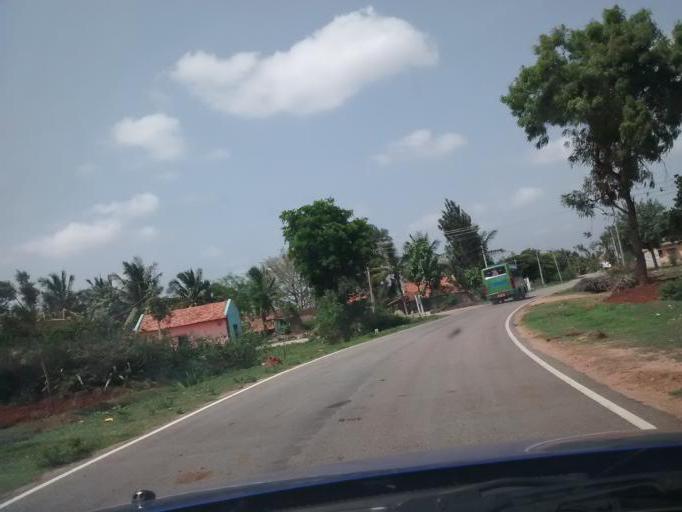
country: IN
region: Karnataka
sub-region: Hassan
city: Hole Narsipur
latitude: 12.6805
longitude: 76.1890
